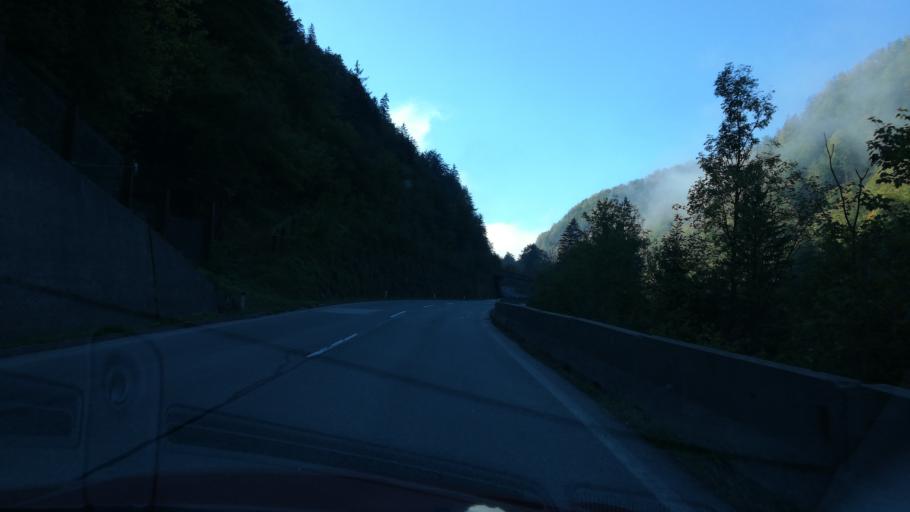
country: AT
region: Styria
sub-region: Politischer Bezirk Liezen
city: Altenmarkt bei Sankt Gallen
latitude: 47.7361
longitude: 14.6518
